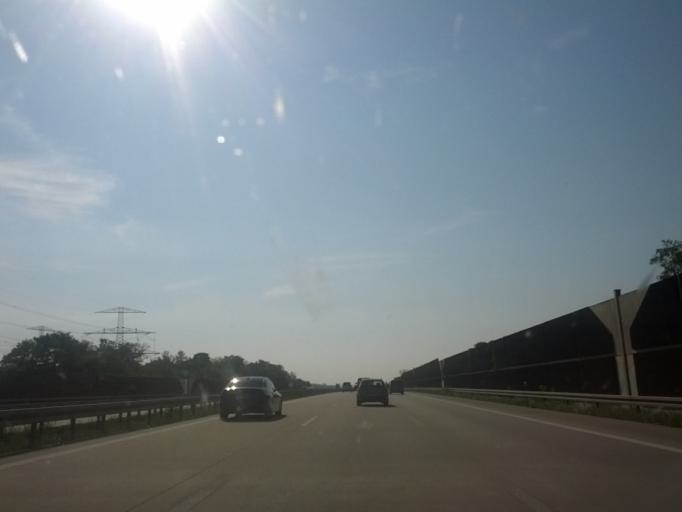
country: DE
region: Brandenburg
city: Neuenhagen
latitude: 52.5371
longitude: 13.7001
